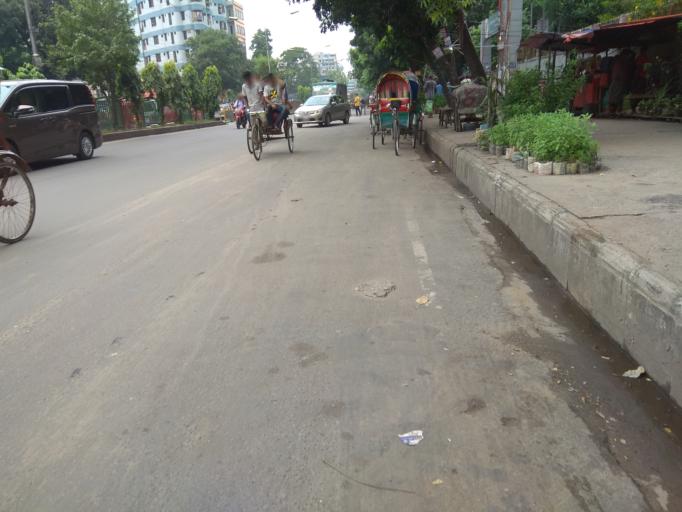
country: BD
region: Dhaka
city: Azimpur
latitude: 23.8020
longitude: 90.3583
